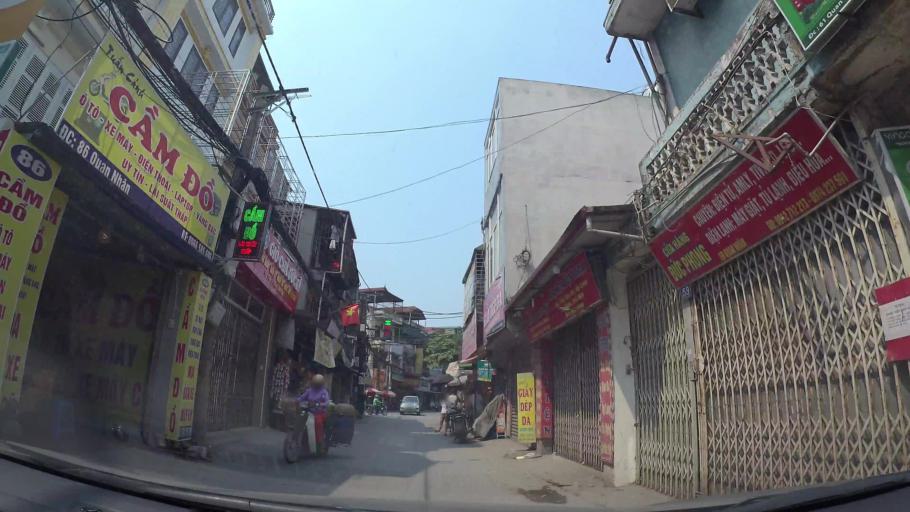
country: VN
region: Ha Noi
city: Thanh Xuan
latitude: 21.0067
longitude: 105.8120
